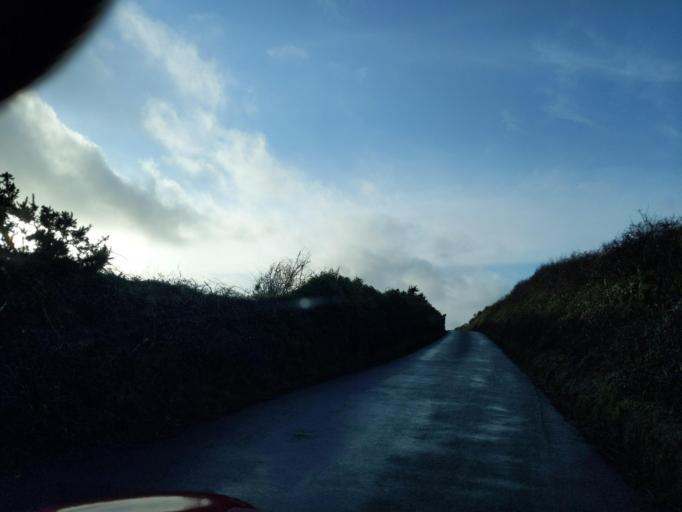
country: GB
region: England
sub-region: Cornwall
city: Fowey
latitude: 50.3311
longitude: -4.6107
